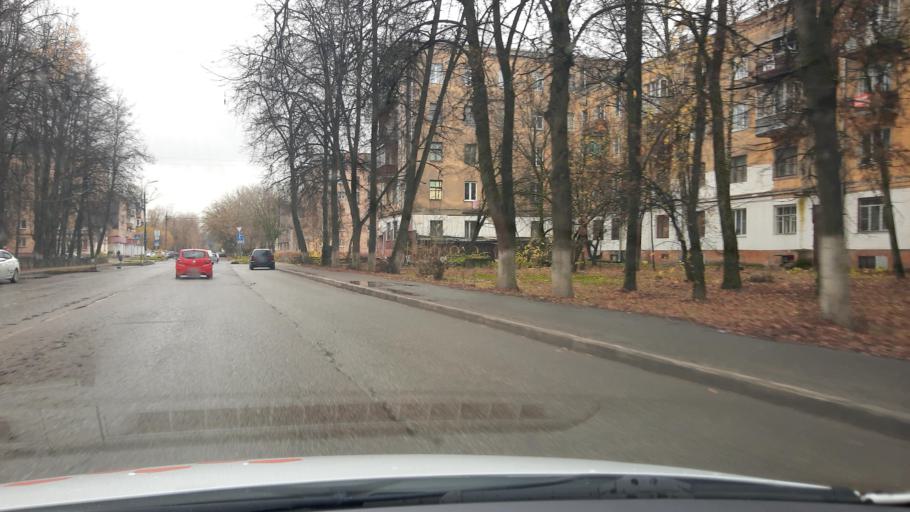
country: RU
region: Moskovskaya
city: Elektrostal'
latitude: 55.7930
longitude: 38.4457
